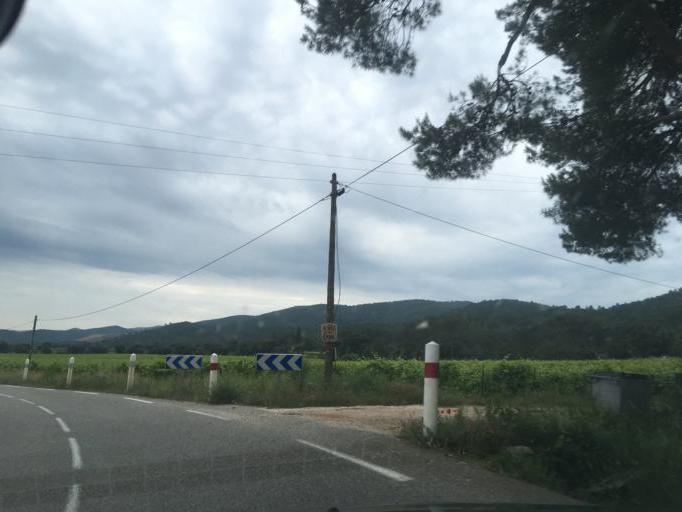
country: FR
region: Provence-Alpes-Cote d'Azur
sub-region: Departement du Var
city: Pierrefeu-du-Var
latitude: 43.2323
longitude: 6.1716
